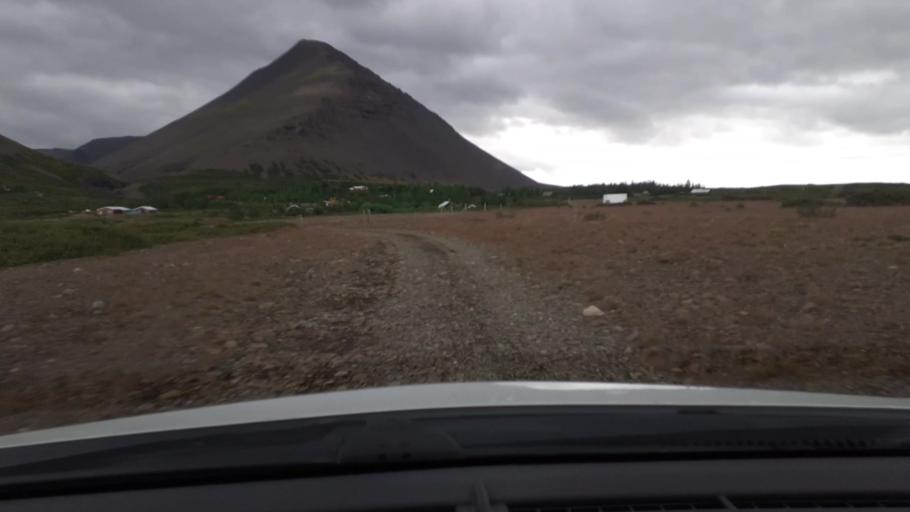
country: IS
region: West
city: Borgarnes
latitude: 64.4600
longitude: -21.9582
